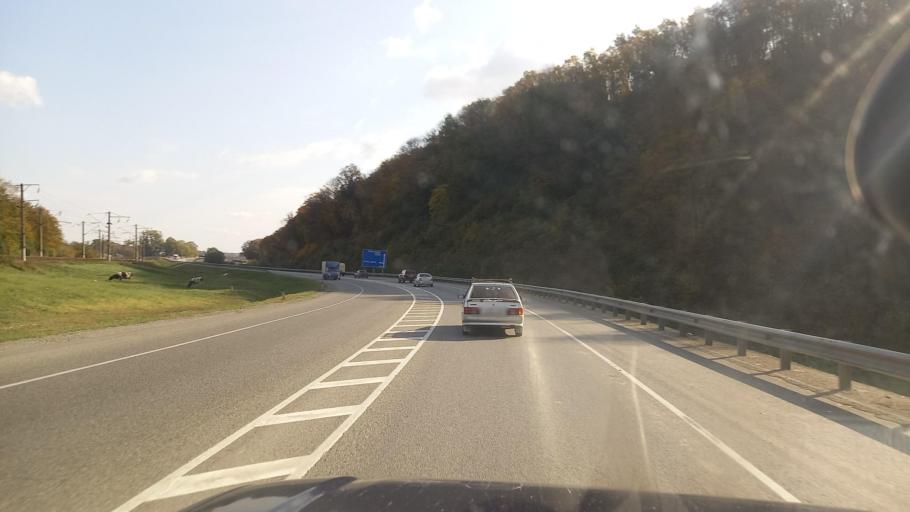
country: RU
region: Krasnodarskiy
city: Krymsk
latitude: 44.8706
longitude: 37.8976
